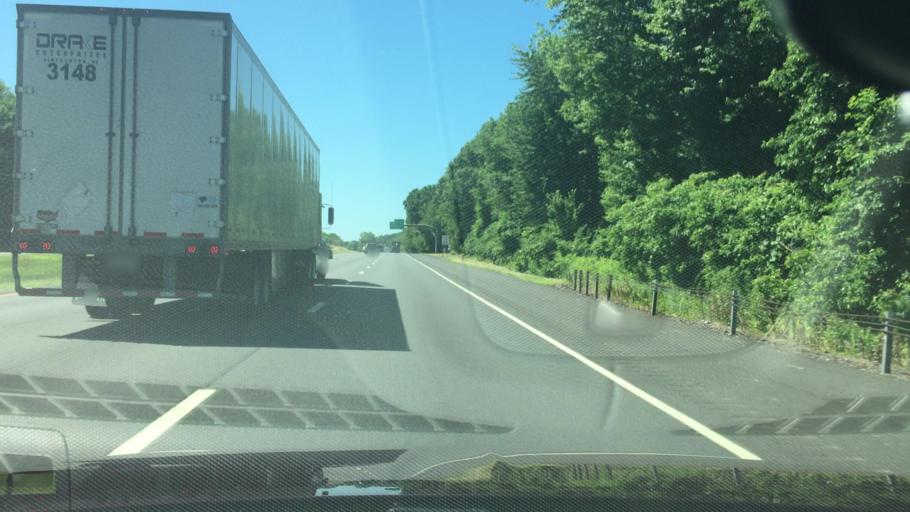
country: US
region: Connecticut
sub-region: Hartford County
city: Bristol
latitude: 41.6060
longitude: -72.9021
